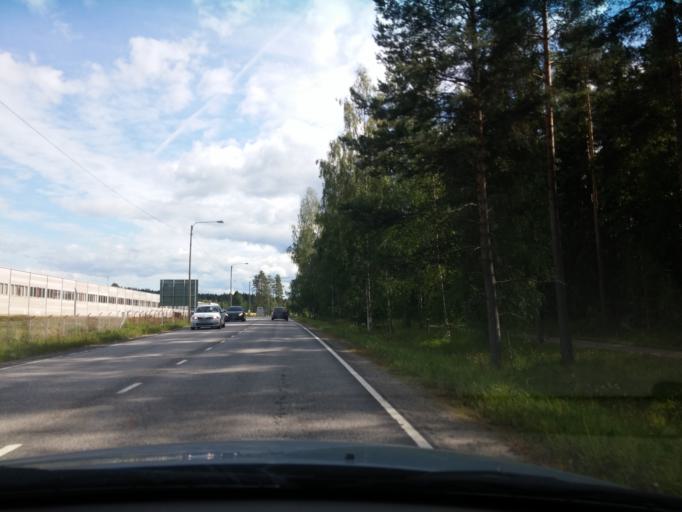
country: FI
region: Central Finland
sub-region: Keuruu
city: Keuruu
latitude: 62.2508
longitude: 24.7225
